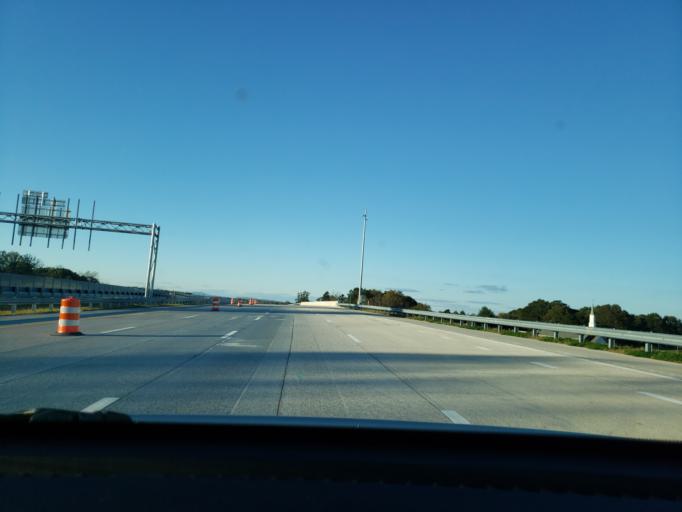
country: US
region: North Carolina
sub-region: Forsyth County
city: Walkertown
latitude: 36.1276
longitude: -80.1296
